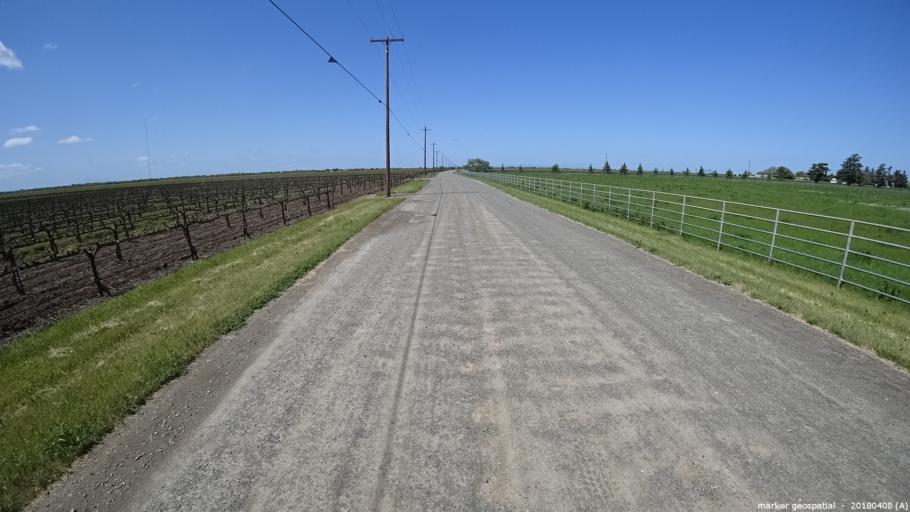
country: US
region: California
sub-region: Sacramento County
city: Walnut Grove
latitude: 38.2988
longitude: -121.4699
